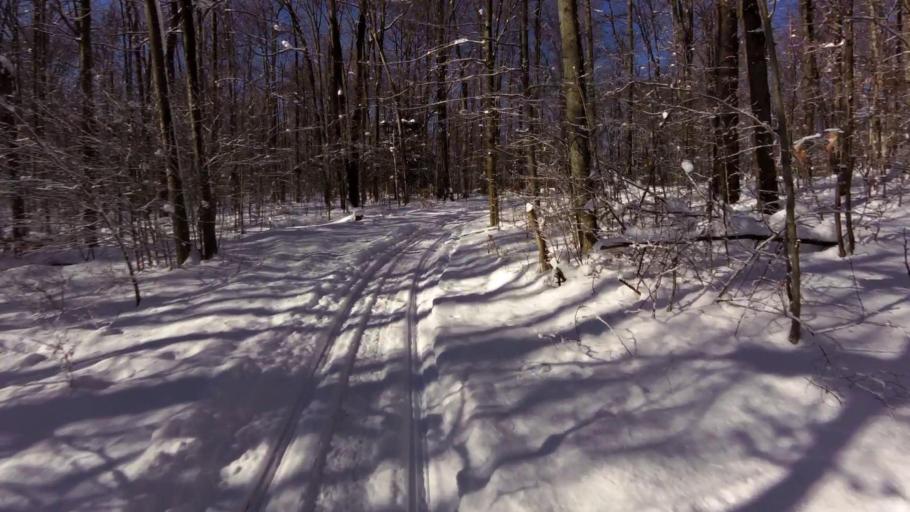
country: US
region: New York
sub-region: Cattaraugus County
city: Salamanca
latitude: 42.0391
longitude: -78.7815
